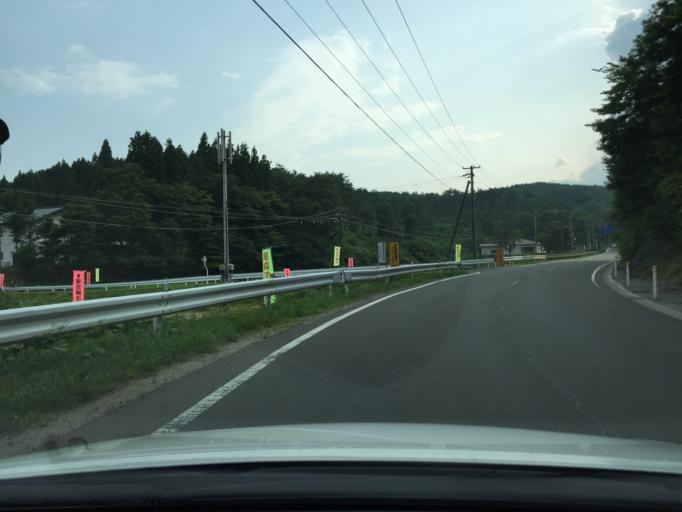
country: JP
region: Miyagi
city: Marumori
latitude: 37.6890
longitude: 140.8040
